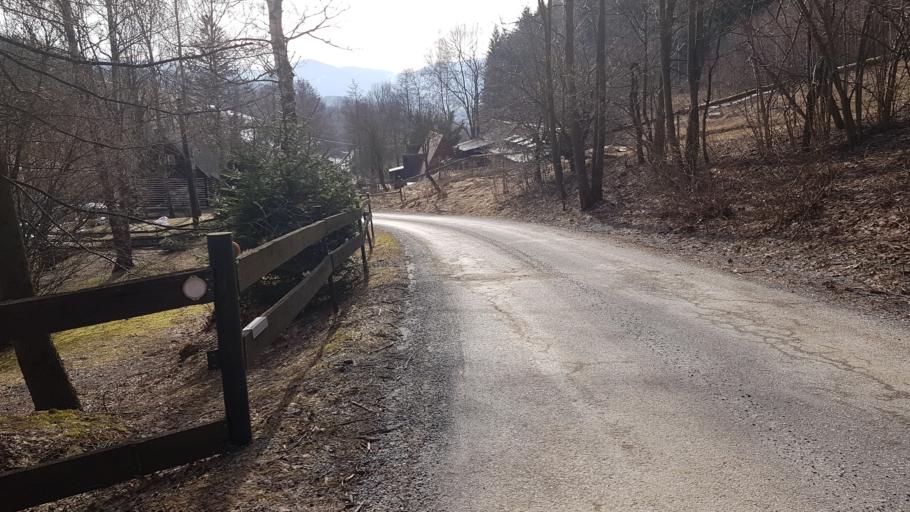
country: CZ
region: Olomoucky
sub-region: Okres Jesenik
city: Jesenik
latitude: 50.2260
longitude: 17.2283
